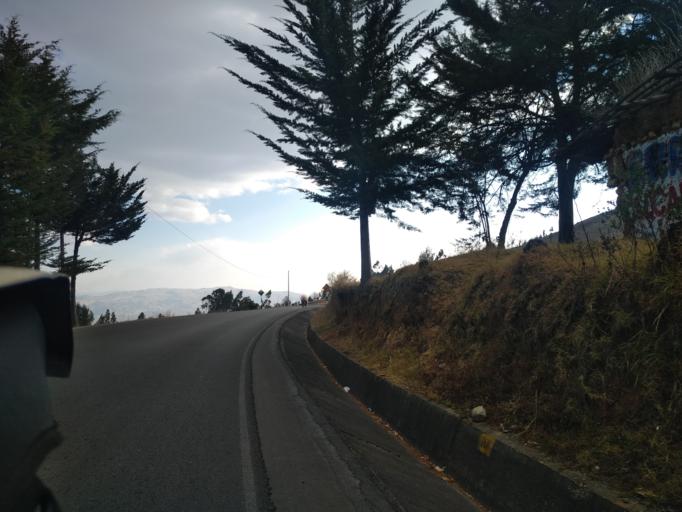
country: PE
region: Cajamarca
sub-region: Provincia de Cajamarca
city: Llacanora
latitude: -7.1481
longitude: -78.4108
